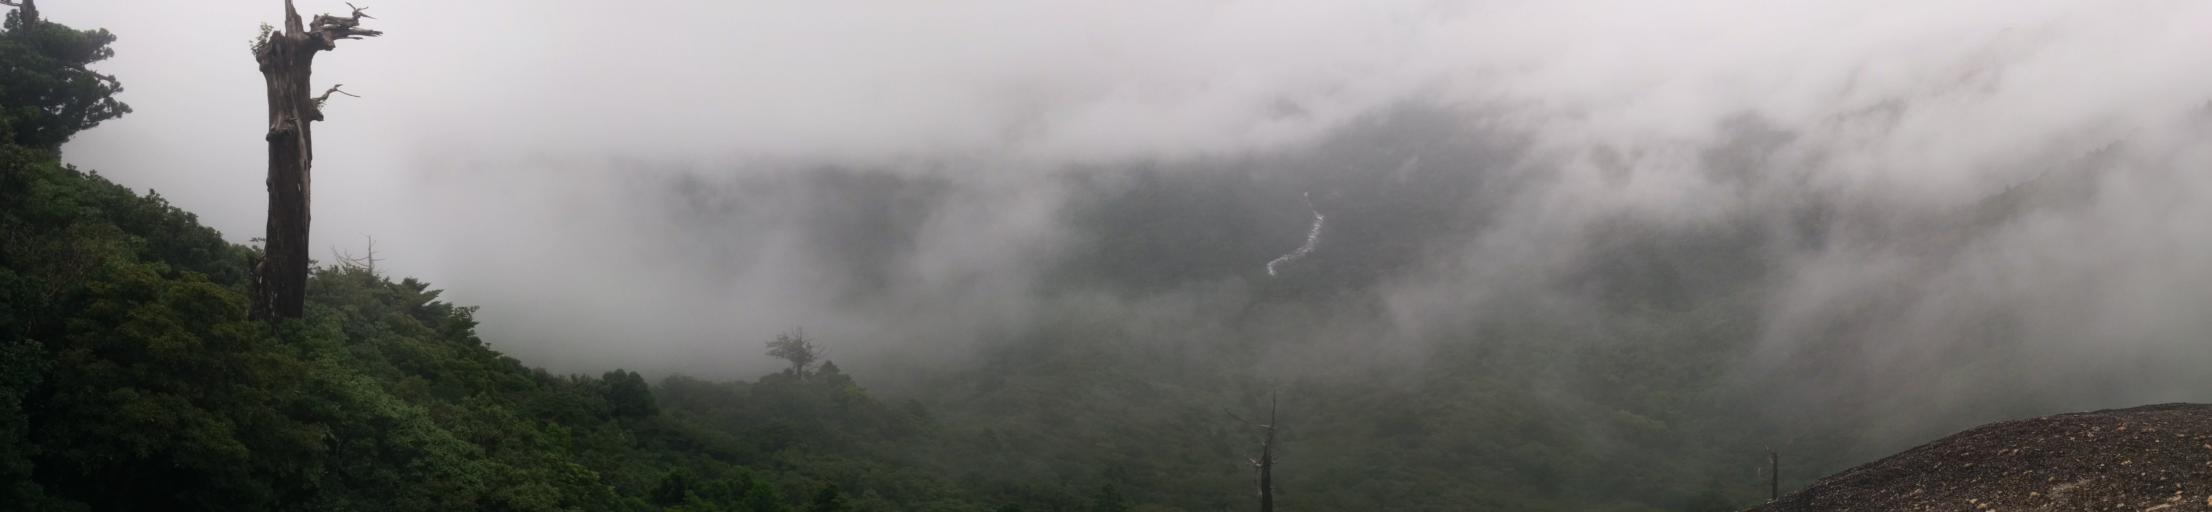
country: JP
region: Kagoshima
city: Nishinoomote
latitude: 30.3623
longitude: 130.5683
